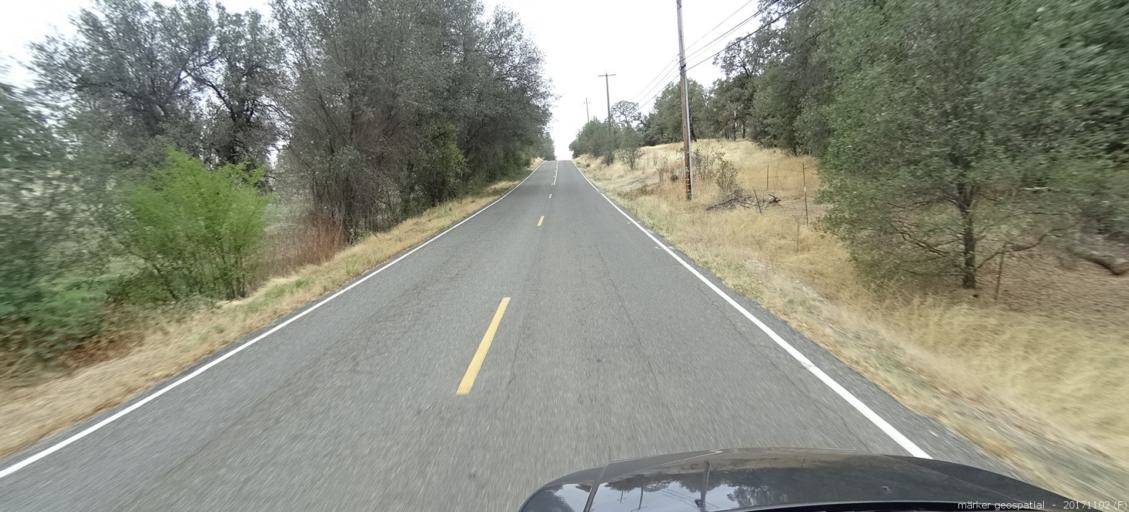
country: US
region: California
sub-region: Shasta County
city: Bella Vista
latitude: 40.6283
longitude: -122.2968
